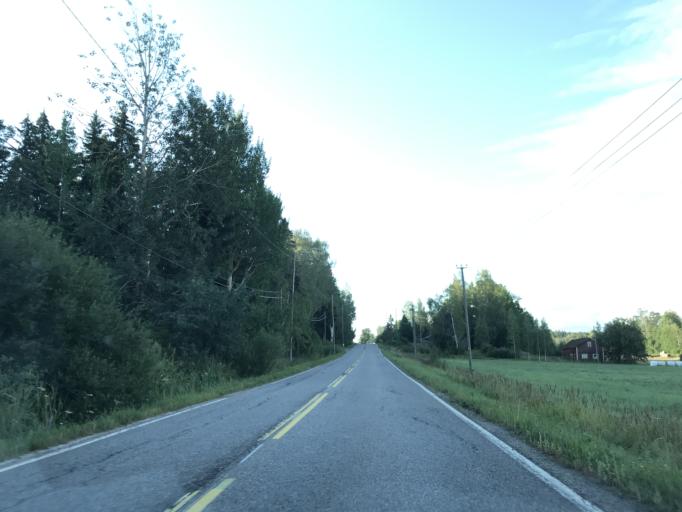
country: FI
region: Uusimaa
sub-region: Helsinki
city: Kauniainen
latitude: 60.3635
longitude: 24.6842
